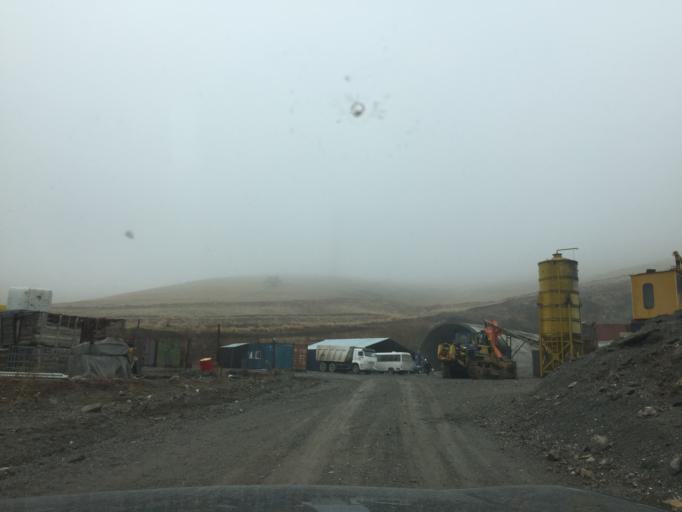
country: KZ
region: Ongtustik Qazaqstan
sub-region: Tulkibas Audany
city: Zhabagly
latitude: 42.5172
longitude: 70.5655
